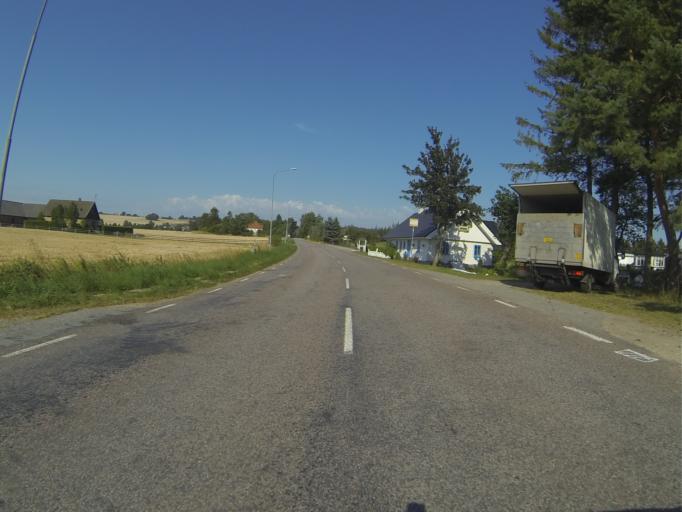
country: SE
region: Skane
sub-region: Hoors Kommun
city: Loberod
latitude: 55.7115
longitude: 13.5183
